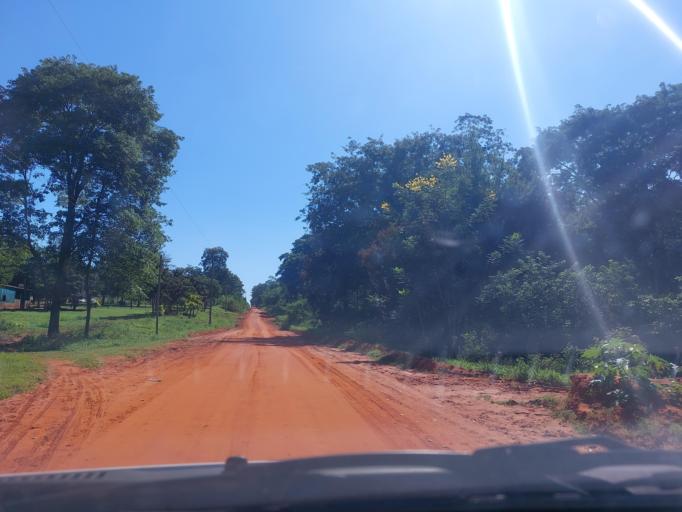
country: PY
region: San Pedro
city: Lima
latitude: -24.1708
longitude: -56.0134
